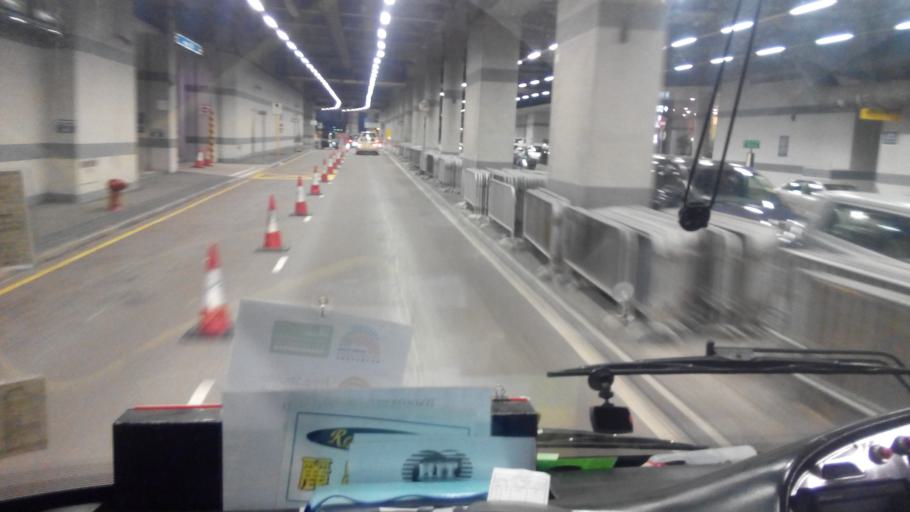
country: HK
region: Wanchai
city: Wan Chai
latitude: 22.2837
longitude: 114.1740
